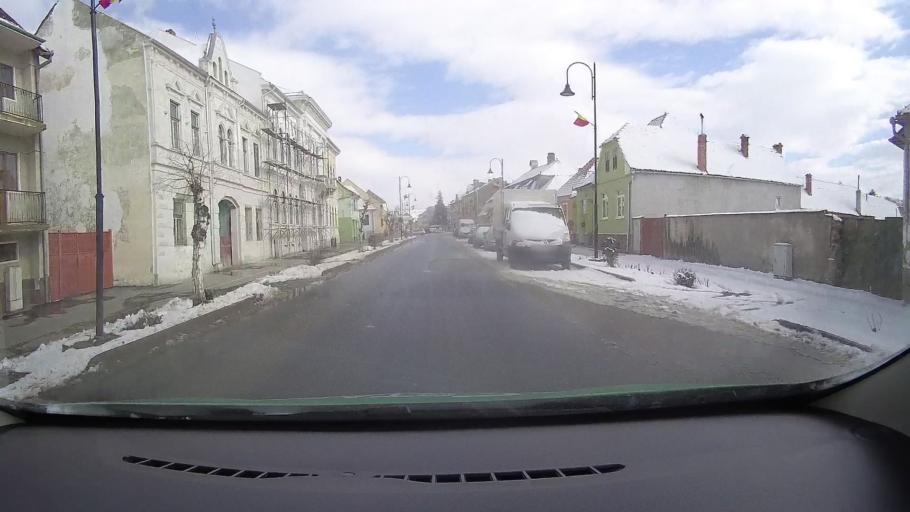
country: RO
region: Sibiu
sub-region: Oras Agnita
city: Agnita
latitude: 45.9757
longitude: 24.6197
